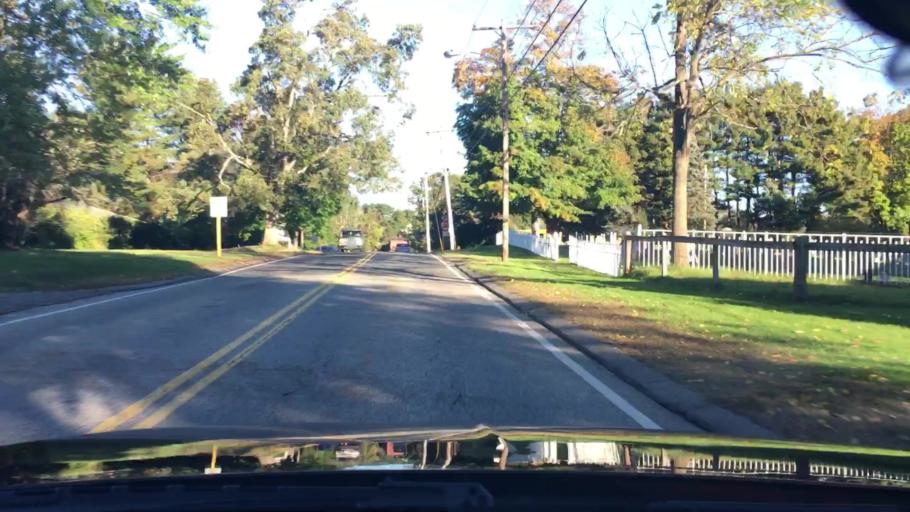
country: US
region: Massachusetts
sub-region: Hampden County
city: East Longmeadow
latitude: 42.0425
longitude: -72.5005
